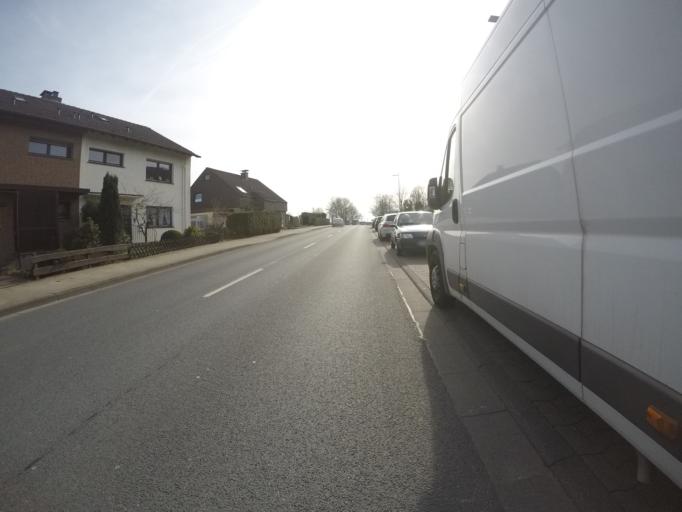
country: DE
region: North Rhine-Westphalia
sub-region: Regierungsbezirk Detmold
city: Bielefeld
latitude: 52.0540
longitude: 8.6024
